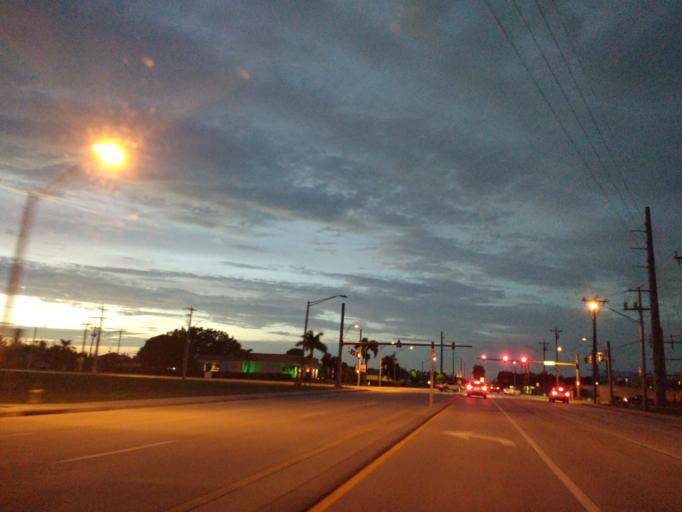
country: US
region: Florida
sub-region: Lee County
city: Cape Coral
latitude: 26.6219
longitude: -81.9743
